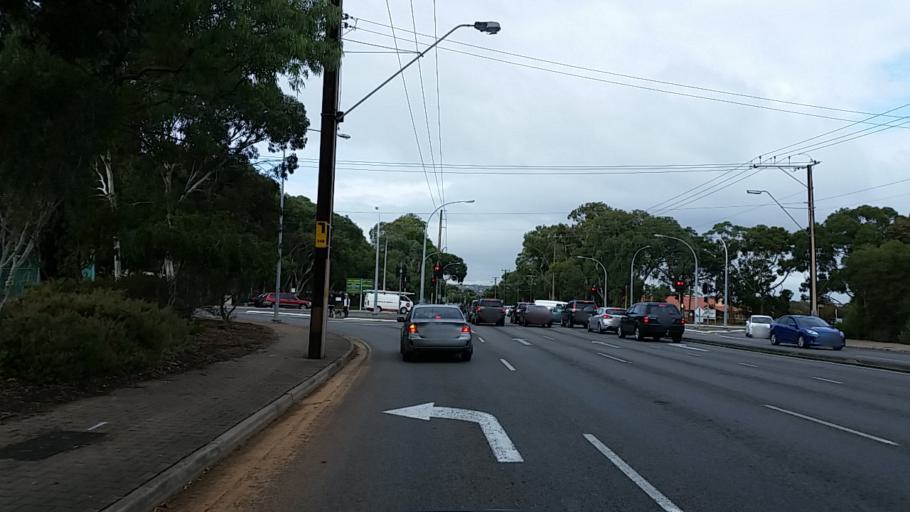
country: AU
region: South Australia
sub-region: Marion
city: Plympton Park
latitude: -34.9954
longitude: 138.5394
